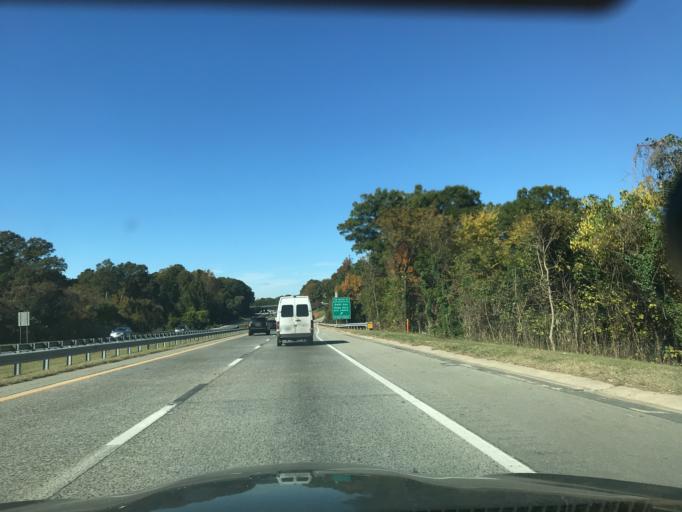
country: US
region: North Carolina
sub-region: Durham County
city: Durham
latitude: 36.0013
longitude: -78.9159
